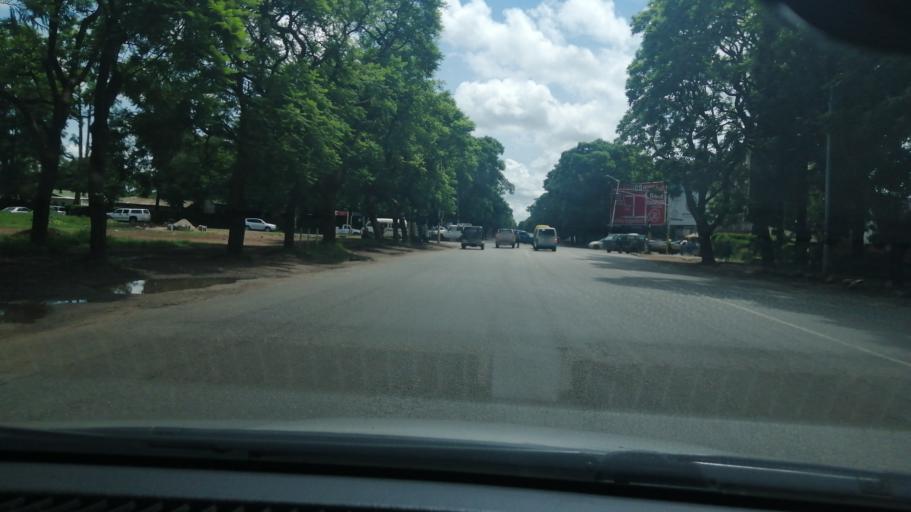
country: ZW
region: Harare
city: Harare
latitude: -17.8186
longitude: 31.0366
